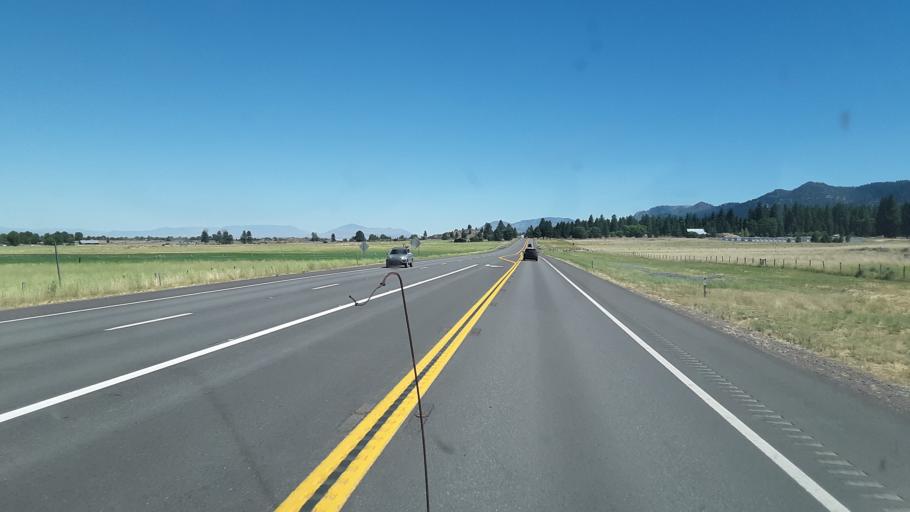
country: US
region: California
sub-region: Lassen County
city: Janesville
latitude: 40.3136
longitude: -120.5379
